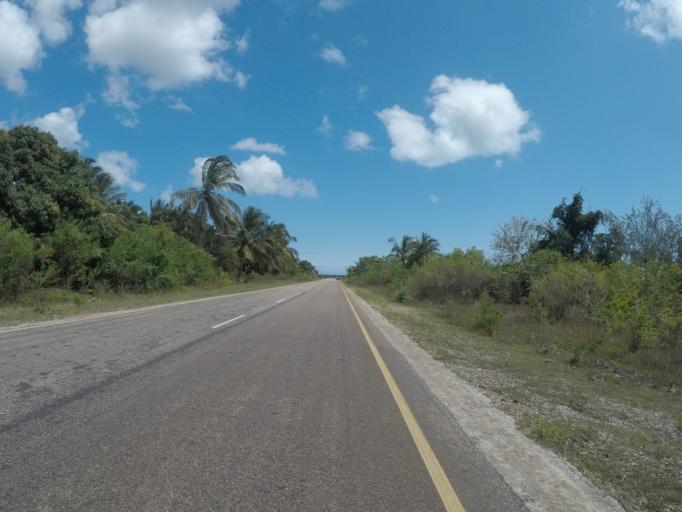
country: TZ
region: Zanzibar Central/South
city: Koani
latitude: -6.2450
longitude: 39.3558
